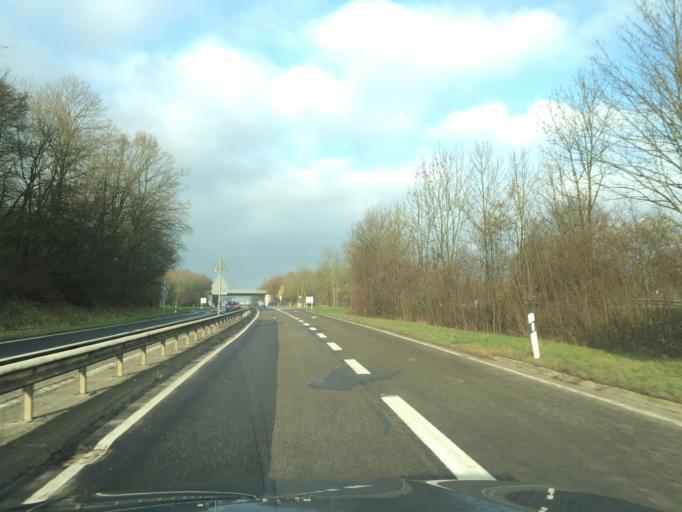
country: DE
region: Rheinland-Pfalz
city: Sinzig
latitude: 50.5649
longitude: 7.2442
